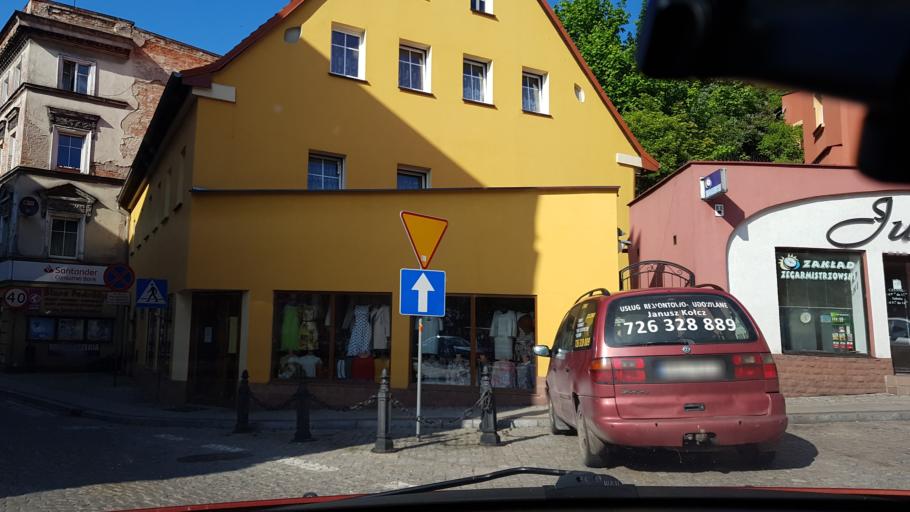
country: PL
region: Lower Silesian Voivodeship
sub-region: Powiat klodzki
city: Nowa Ruda
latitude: 50.5807
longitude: 16.5011
